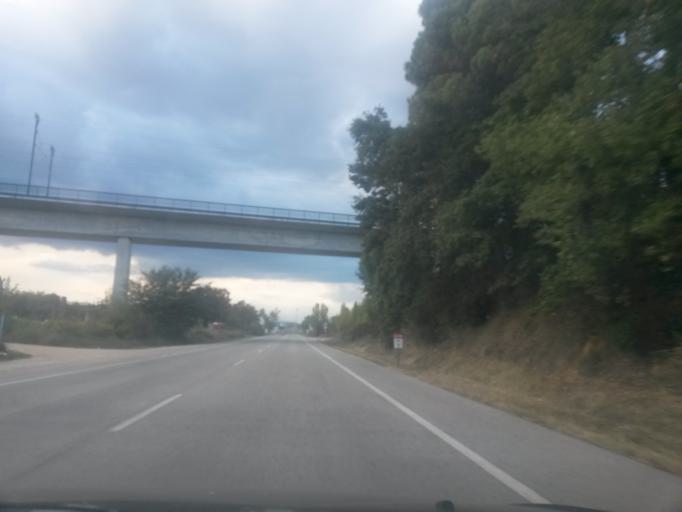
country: ES
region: Catalonia
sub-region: Provincia de Girona
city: Vilobi d'Onyar
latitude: 41.8964
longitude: 2.7735
